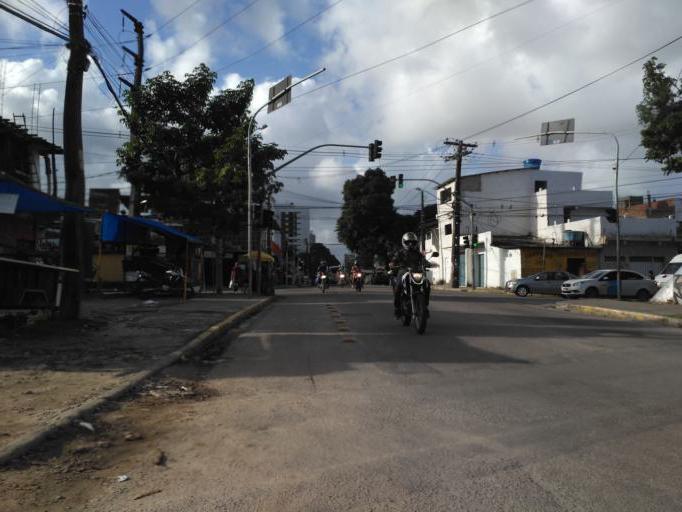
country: BR
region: Pernambuco
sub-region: Recife
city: Recife
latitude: -8.0470
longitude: -34.9405
